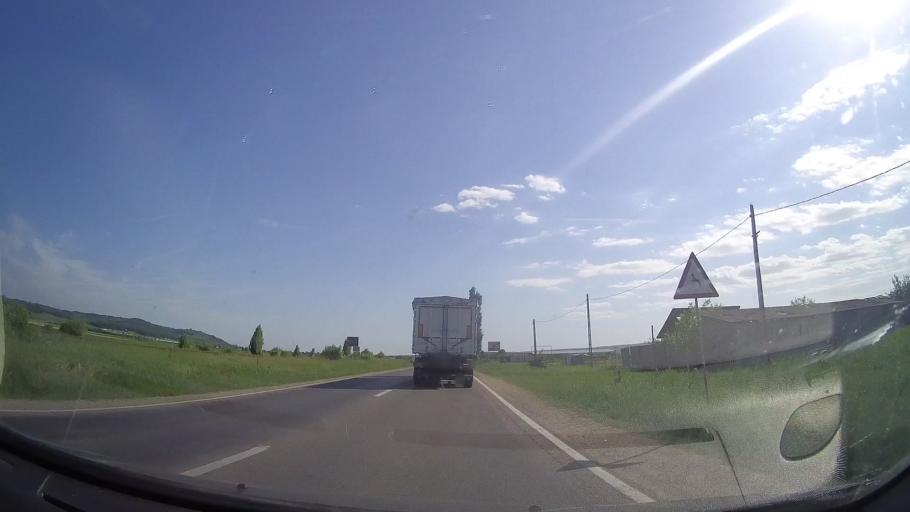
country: RO
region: Prahova
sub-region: Comuna Magurele
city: Magurele
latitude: 45.0793
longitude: 26.0316
